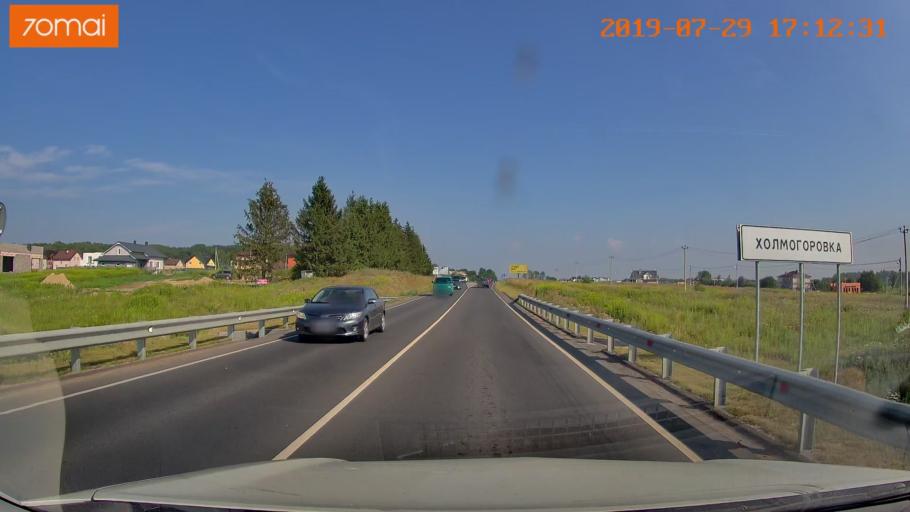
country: RU
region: Kaliningrad
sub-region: Gorod Kaliningrad
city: Kaliningrad
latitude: 54.7879
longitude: 20.3989
